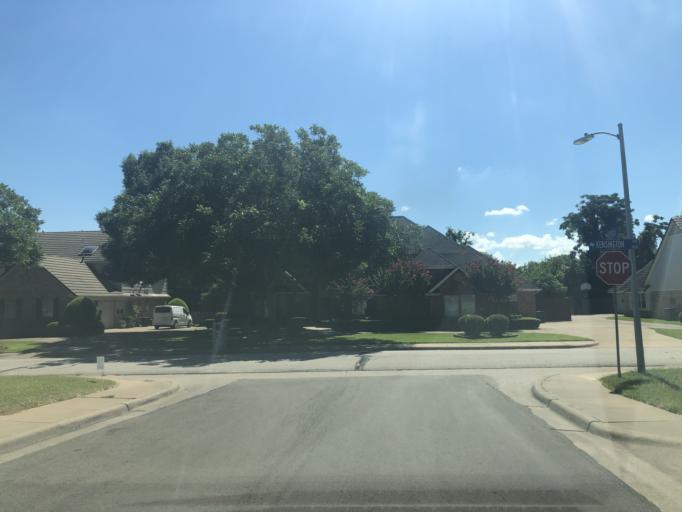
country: US
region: Texas
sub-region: Dallas County
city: Duncanville
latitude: 32.6440
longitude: -96.9282
